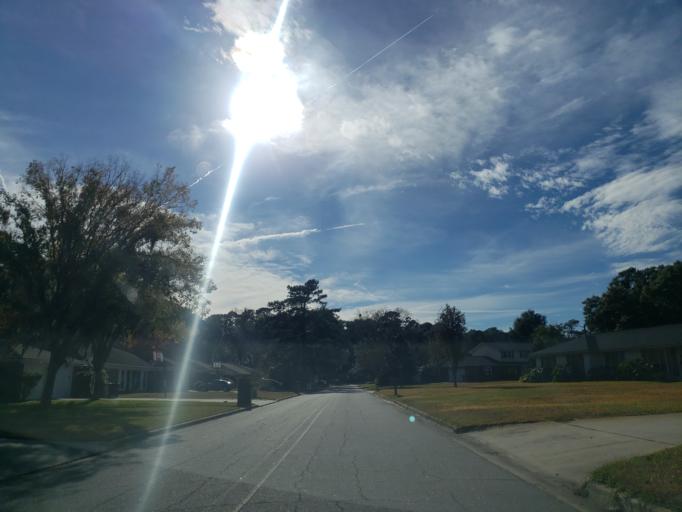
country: US
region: Georgia
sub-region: Chatham County
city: Isle of Hope
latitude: 31.9886
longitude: -81.0937
